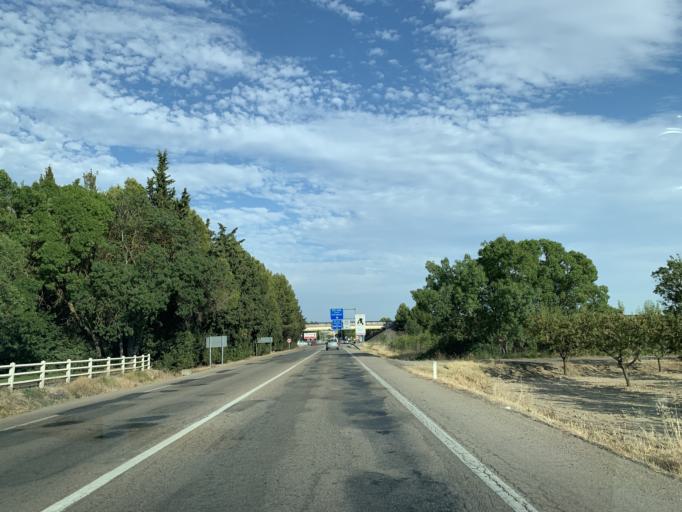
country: ES
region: Aragon
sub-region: Provincia de Huesca
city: Huesca
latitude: 42.1499
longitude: -0.4287
